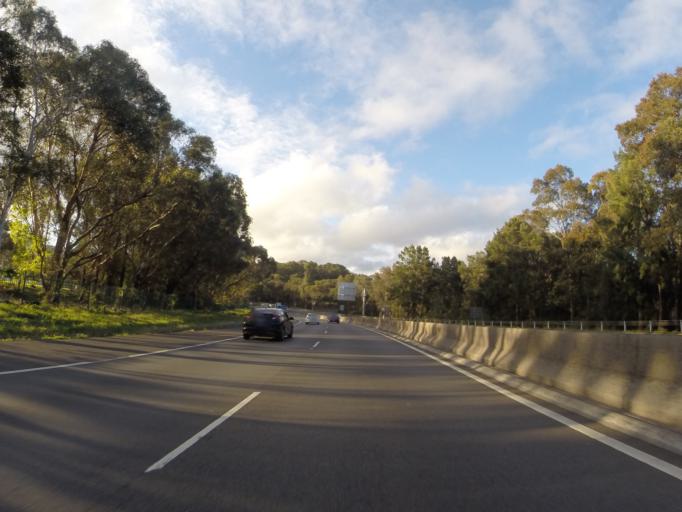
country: AU
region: New South Wales
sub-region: Wollongong
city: Mount Ousley
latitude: -34.4057
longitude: 150.8838
